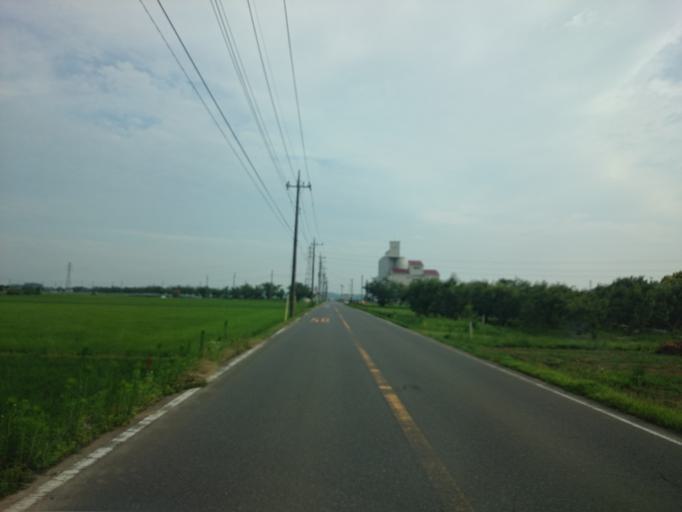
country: JP
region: Ibaraki
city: Tsukuba
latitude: 36.1682
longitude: 140.0989
